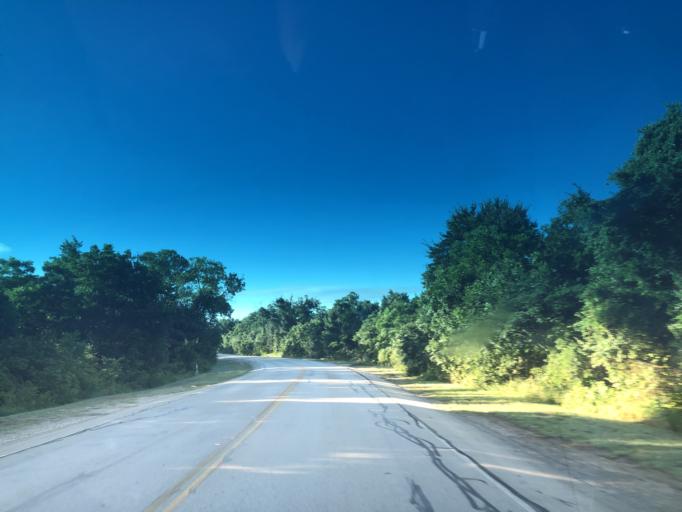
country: US
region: Texas
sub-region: Dallas County
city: Grand Prairie
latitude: 32.7802
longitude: -97.0163
